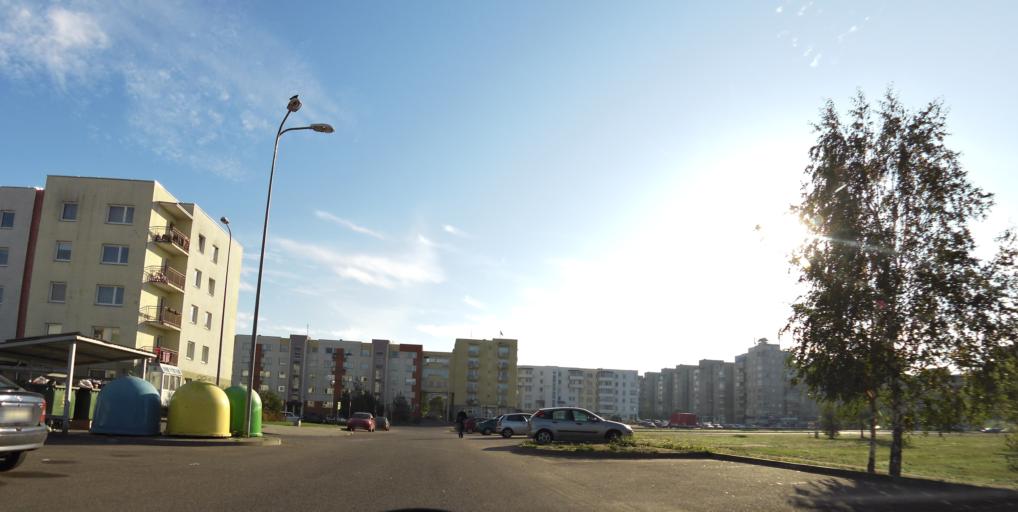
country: LT
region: Vilnius County
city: Pilaite
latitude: 54.7083
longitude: 25.1737
